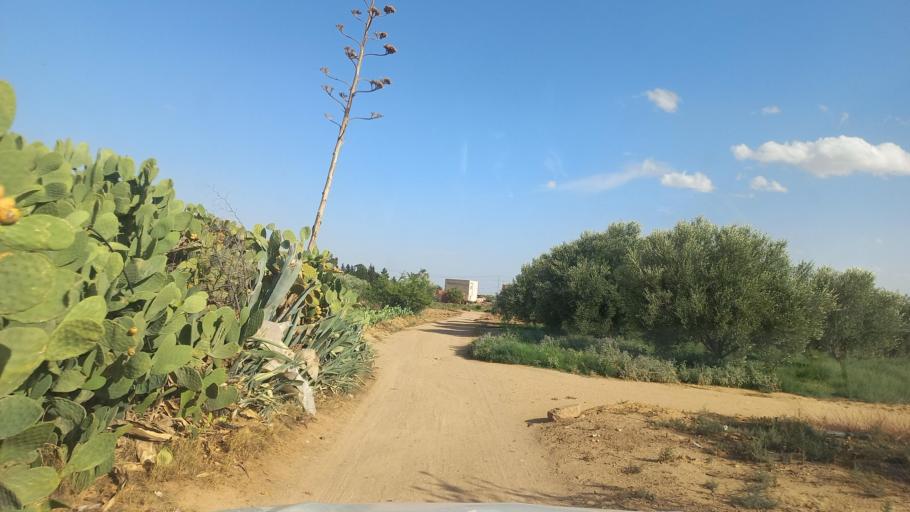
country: TN
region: Al Qasrayn
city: Kasserine
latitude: 35.2587
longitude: 9.0274
